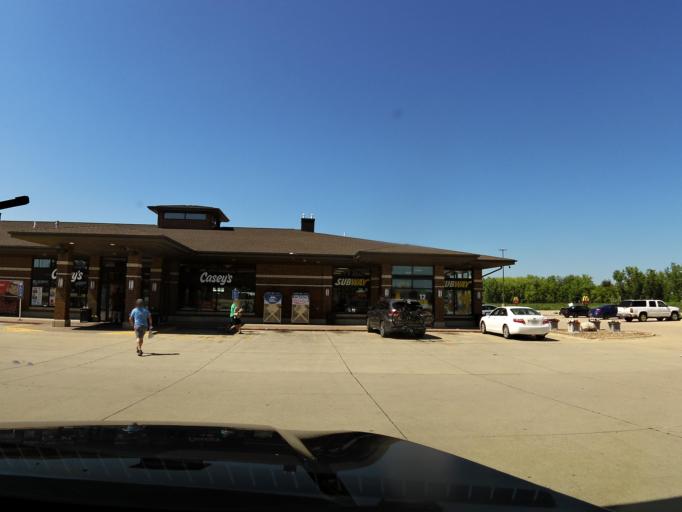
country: US
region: Iowa
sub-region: Linn County
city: Center Point
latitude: 42.1728
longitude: -91.7769
